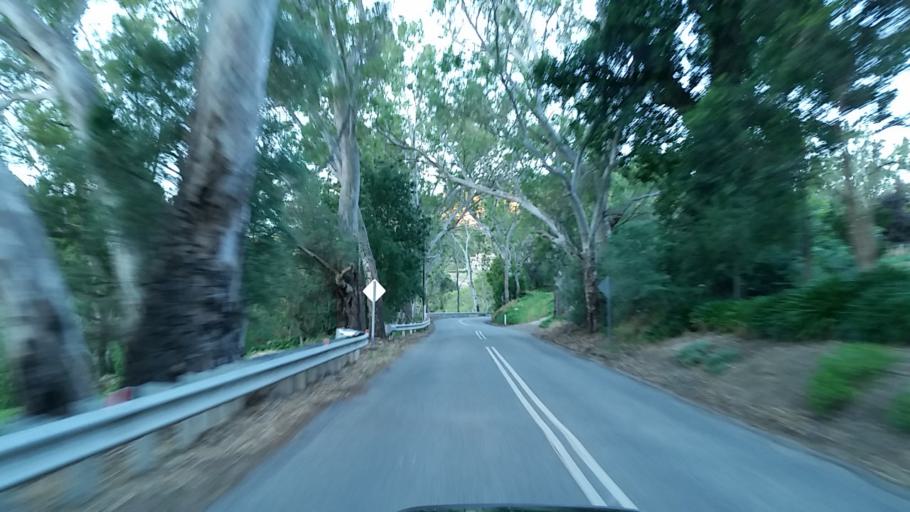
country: AU
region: South Australia
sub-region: Campbelltown
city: Athelstone
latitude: -34.8682
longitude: 138.7564
